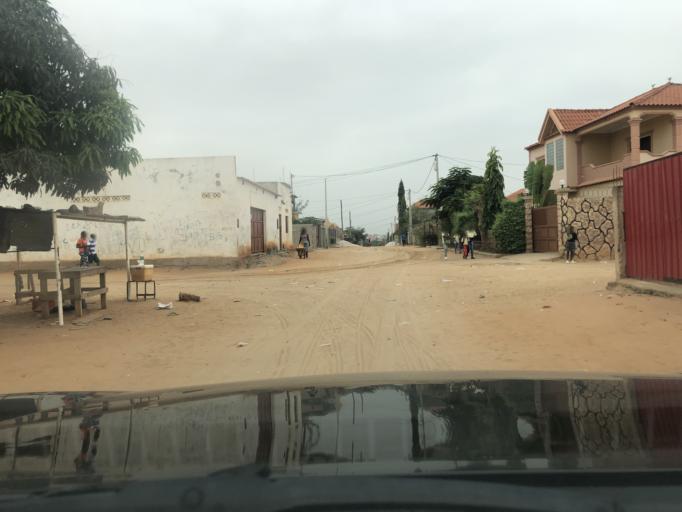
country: AO
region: Luanda
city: Luanda
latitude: -8.9380
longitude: 13.2330
